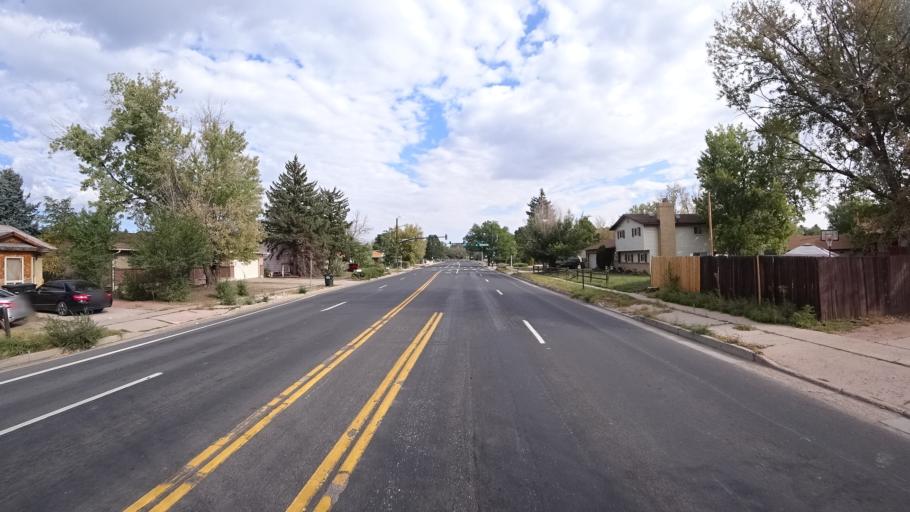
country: US
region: Colorado
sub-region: El Paso County
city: Cimarron Hills
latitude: 38.8500
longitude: -104.7479
